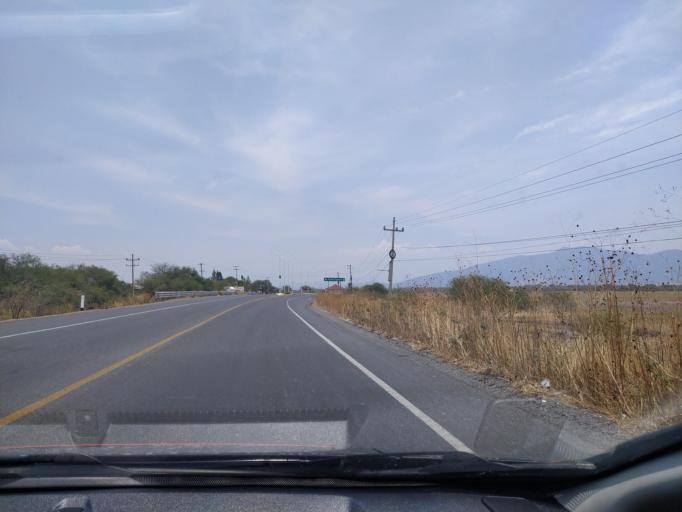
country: MX
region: Jalisco
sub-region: Zacoalco de Torres
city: Barranca de Otates (Barranca de Otatan)
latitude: 20.2936
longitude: -103.6015
